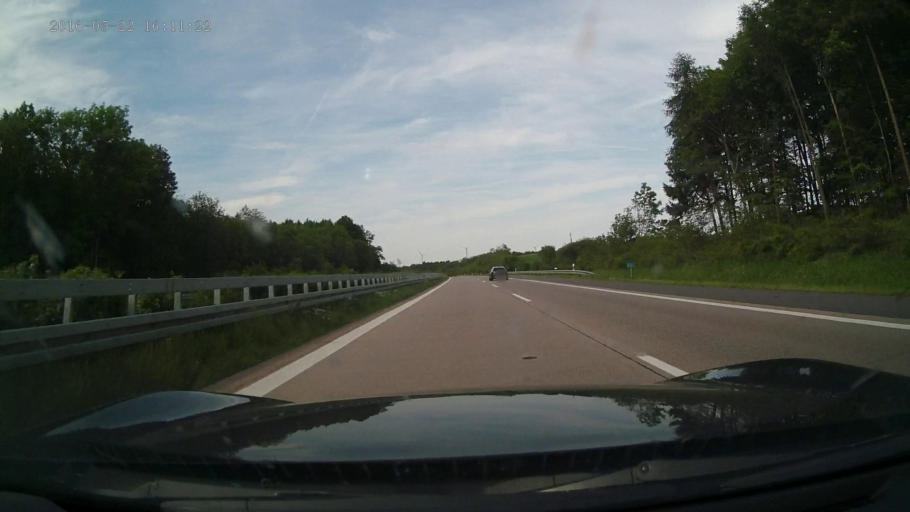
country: DE
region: Baden-Wuerttemberg
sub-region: Karlsruhe Region
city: Osterburken
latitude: 49.3875
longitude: 9.4669
